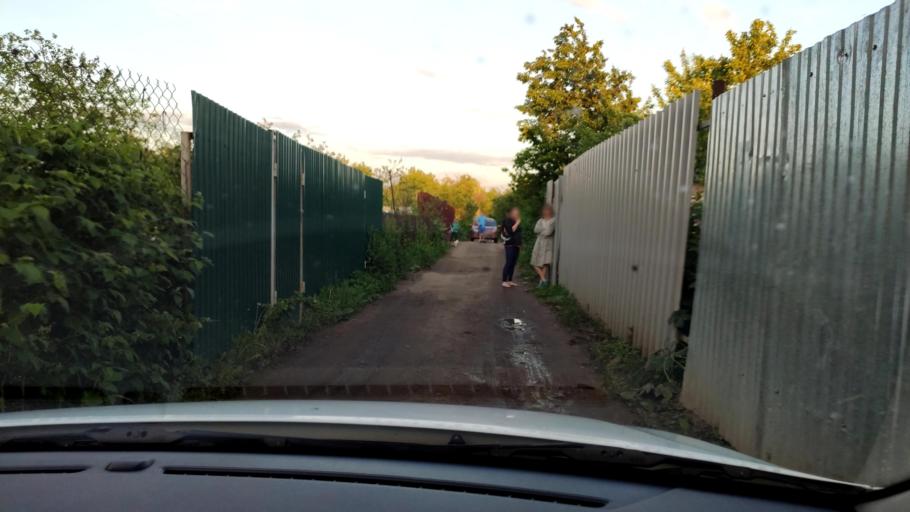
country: RU
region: Tatarstan
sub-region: Gorod Kazan'
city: Kazan
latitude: 55.7273
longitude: 49.1026
